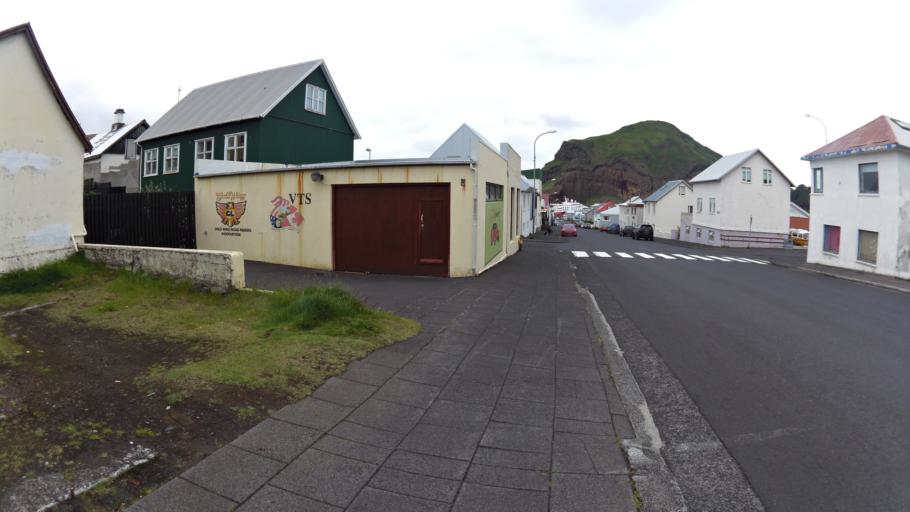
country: IS
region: South
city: Vestmannaeyjar
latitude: 63.4383
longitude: -20.2714
